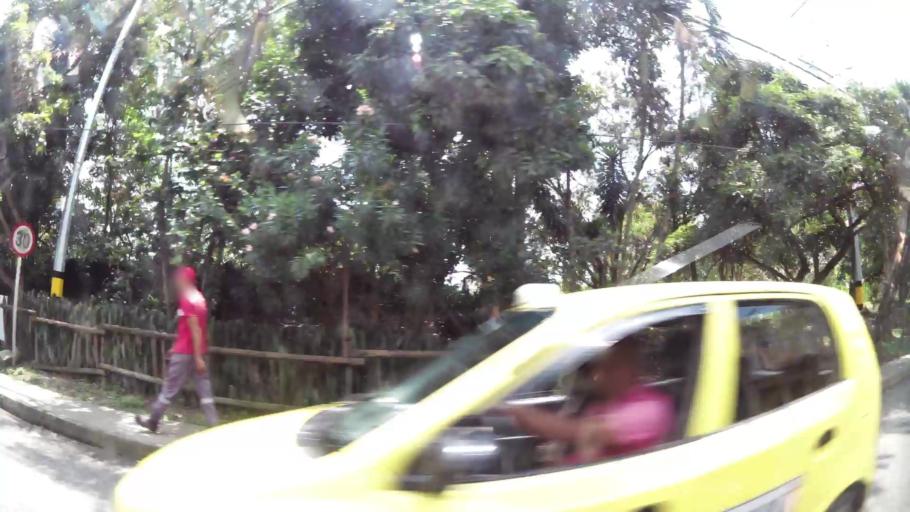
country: CO
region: Antioquia
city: Itagui
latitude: 6.1747
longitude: -75.6136
